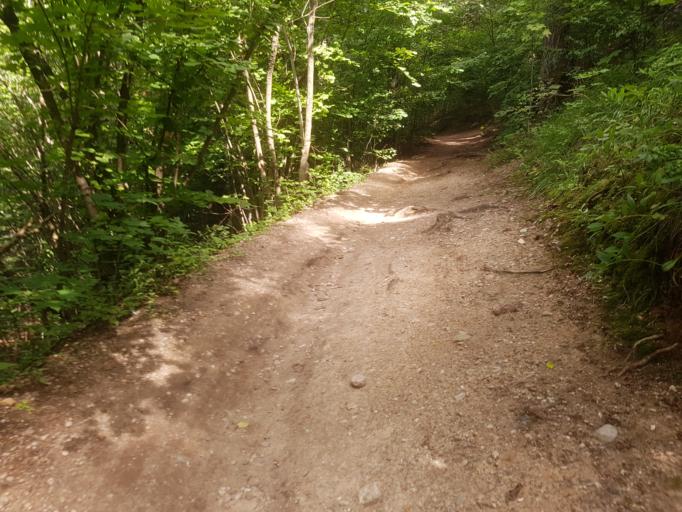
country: LT
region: Vilnius County
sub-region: Vilnius
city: Fabijoniskes
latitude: 54.7875
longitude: 25.3382
